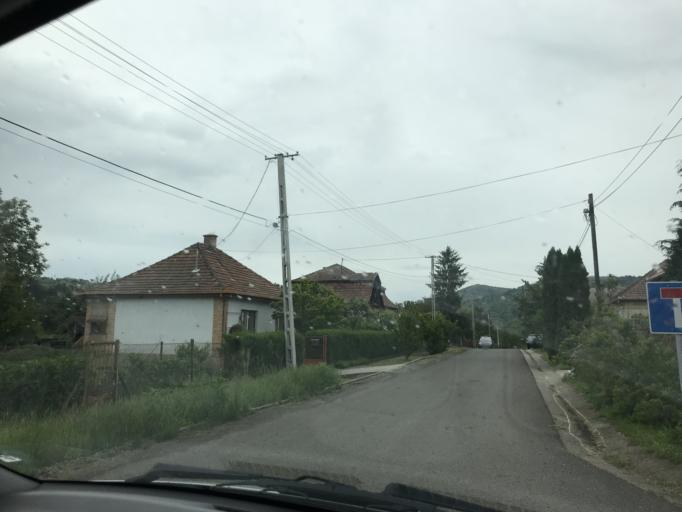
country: HU
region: Nograd
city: Batonyterenye
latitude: 47.9697
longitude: 19.8213
